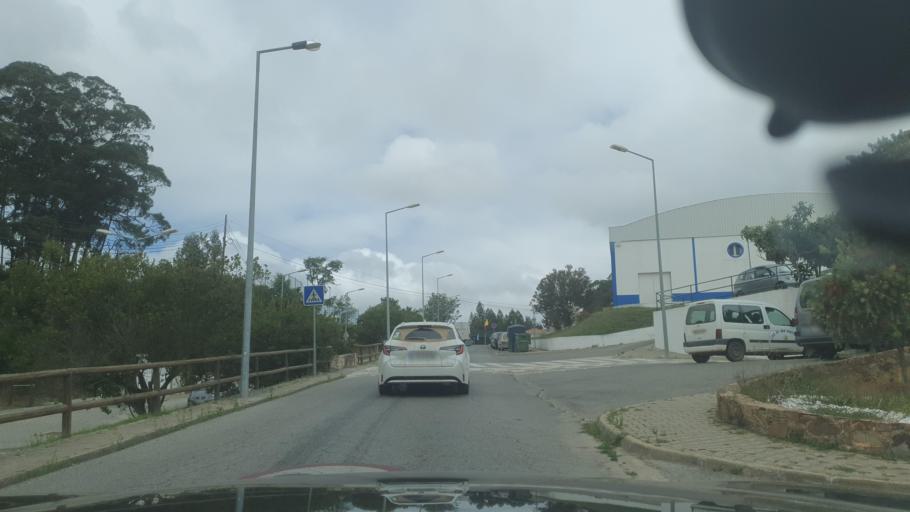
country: PT
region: Beja
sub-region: Odemira
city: Sao Teotonio
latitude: 37.5085
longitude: -8.7090
